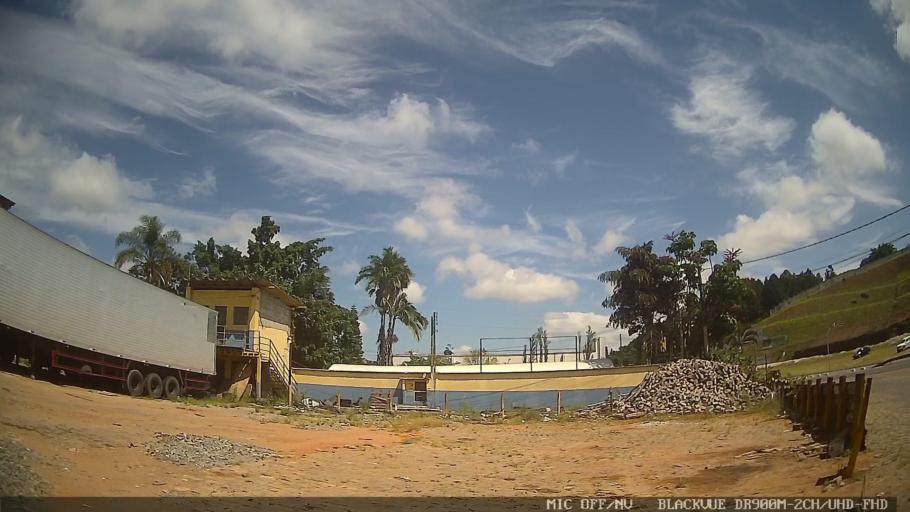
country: BR
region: Sao Paulo
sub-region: Braganca Paulista
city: Braganca Paulista
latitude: -22.9941
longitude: -46.5618
